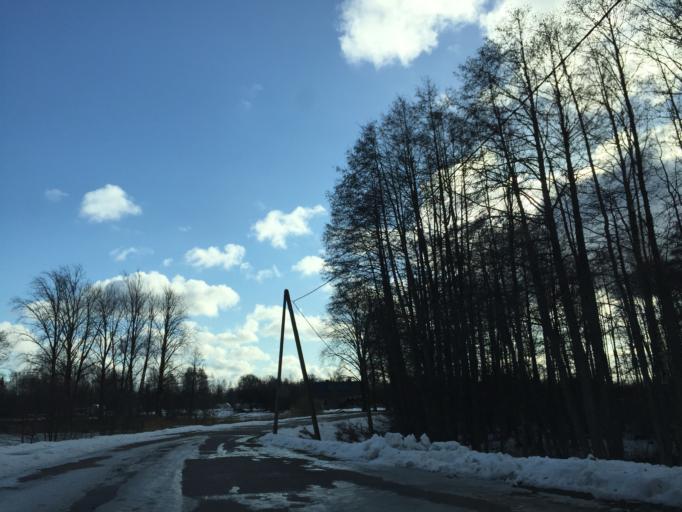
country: LV
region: Limbazu Rajons
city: Limbazi
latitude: 57.6163
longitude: 24.6107
